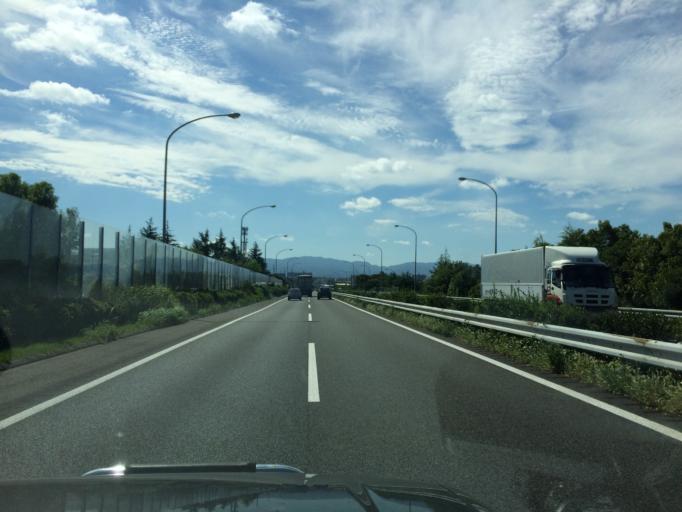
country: JP
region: Osaka
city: Takaishi
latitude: 34.5116
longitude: 135.4900
